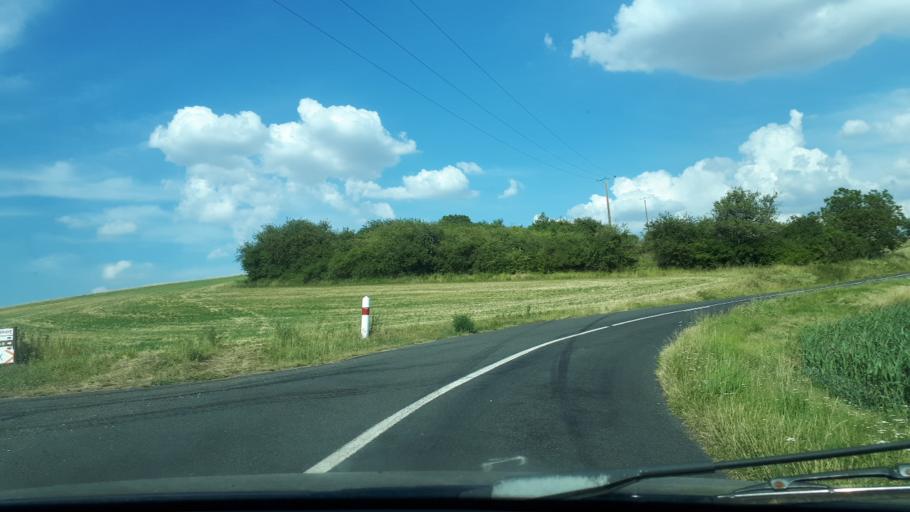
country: FR
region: Pays de la Loire
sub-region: Departement de la Sarthe
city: Besse-sur-Braye
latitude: 47.7794
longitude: 0.7838
